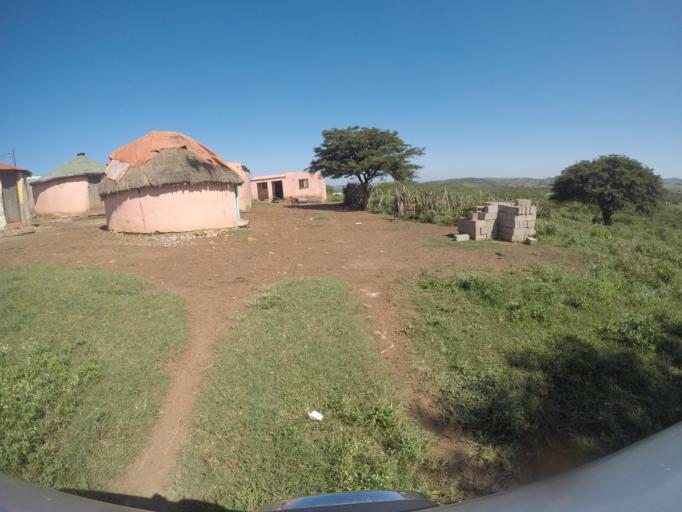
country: ZA
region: KwaZulu-Natal
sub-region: uThungulu District Municipality
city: Empangeni
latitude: -28.5700
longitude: 31.6989
